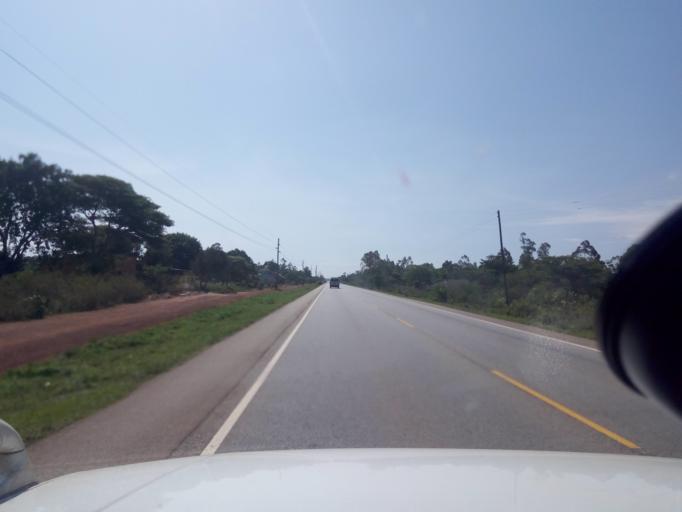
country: UG
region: Eastern Region
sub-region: Bugiri District
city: Bugiri
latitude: 0.5377
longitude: 33.9063
